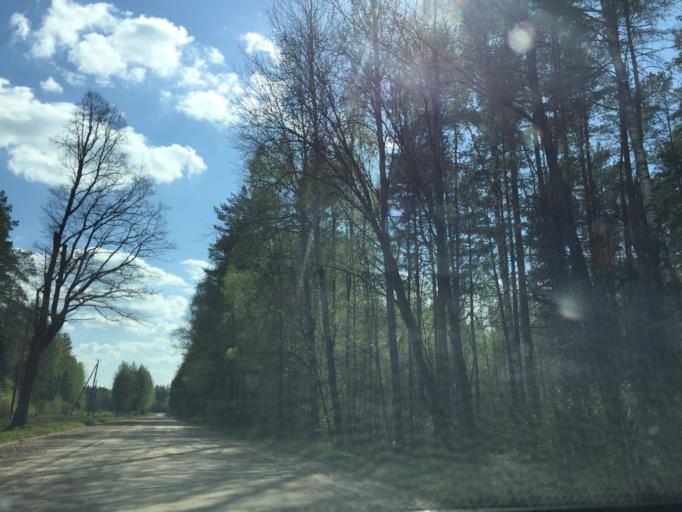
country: LV
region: Vecumnieki
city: Vecumnieki
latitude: 56.4816
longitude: 24.5346
